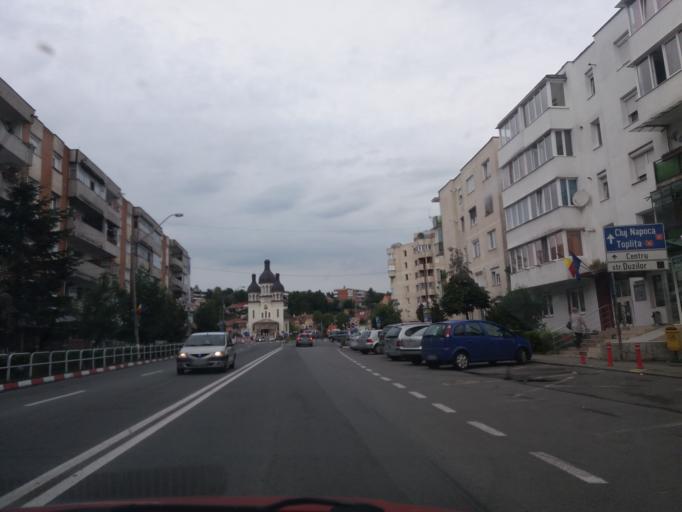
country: RO
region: Mures
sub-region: Municipiul Reghin
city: Reghin
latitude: 46.7735
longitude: 24.7026
